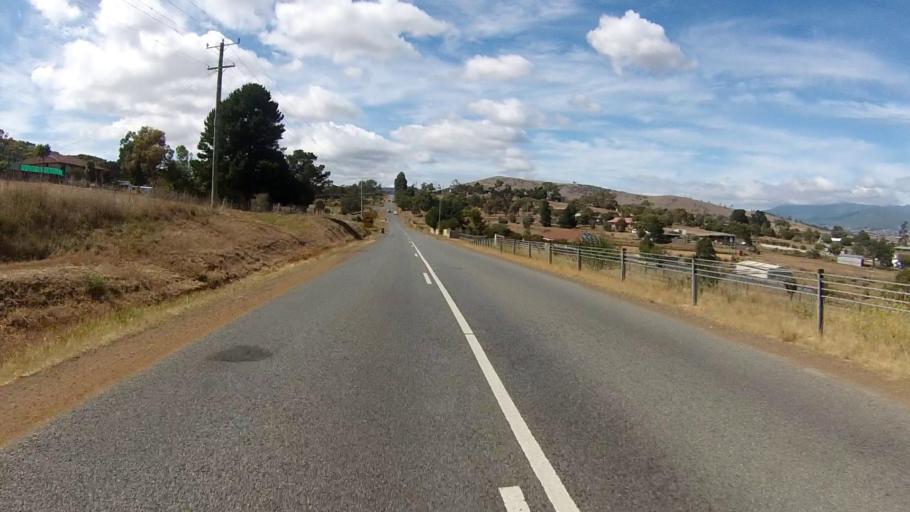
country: AU
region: Tasmania
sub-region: Brighton
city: Bridgewater
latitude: -42.7100
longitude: 147.2694
